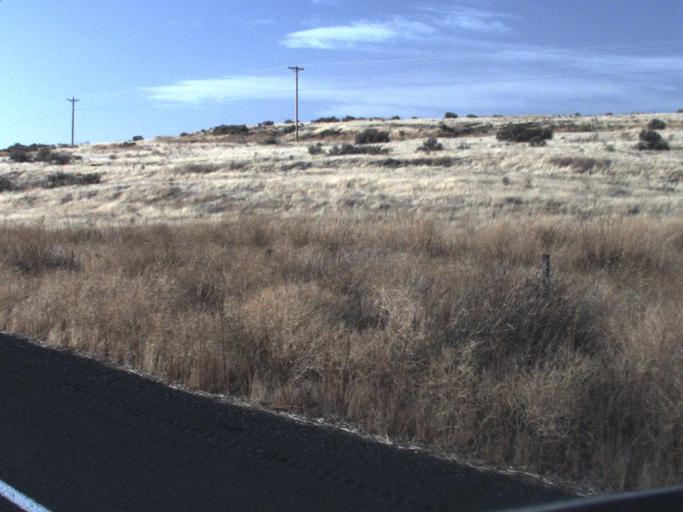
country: US
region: Washington
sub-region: Adams County
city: Ritzville
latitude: 47.3477
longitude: -118.5690
